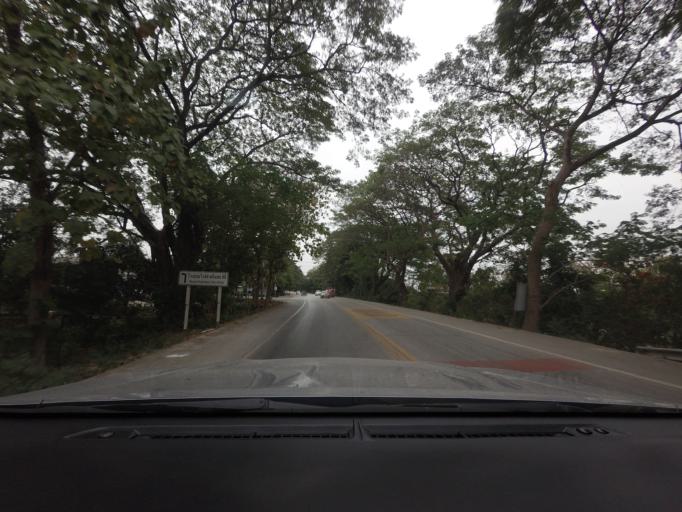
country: TH
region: Lamphun
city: Lamphun
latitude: 18.6109
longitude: 99.0298
